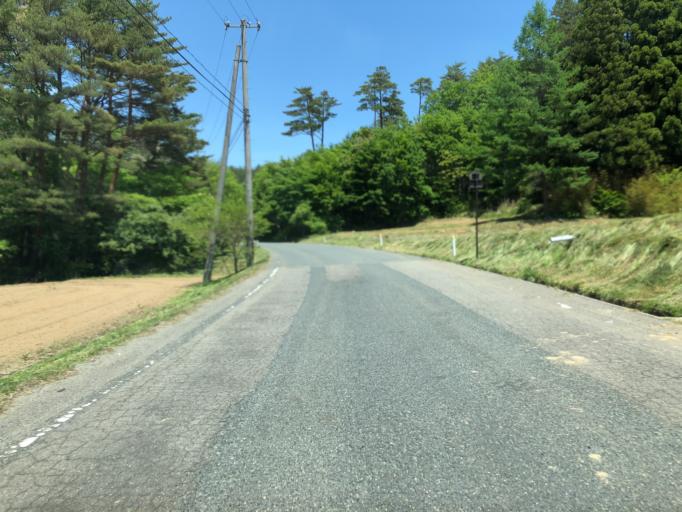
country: JP
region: Fukushima
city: Funehikimachi-funehiki
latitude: 37.5201
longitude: 140.7777
